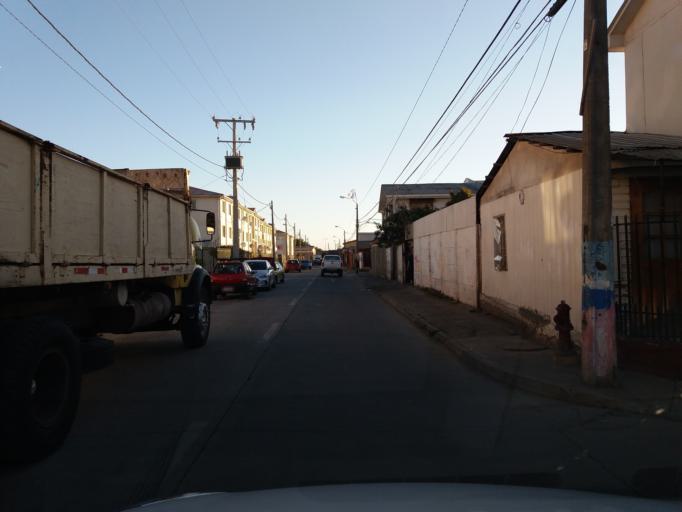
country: CL
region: Valparaiso
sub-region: Provincia de Quillota
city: Quillota
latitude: -32.8939
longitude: -71.2600
